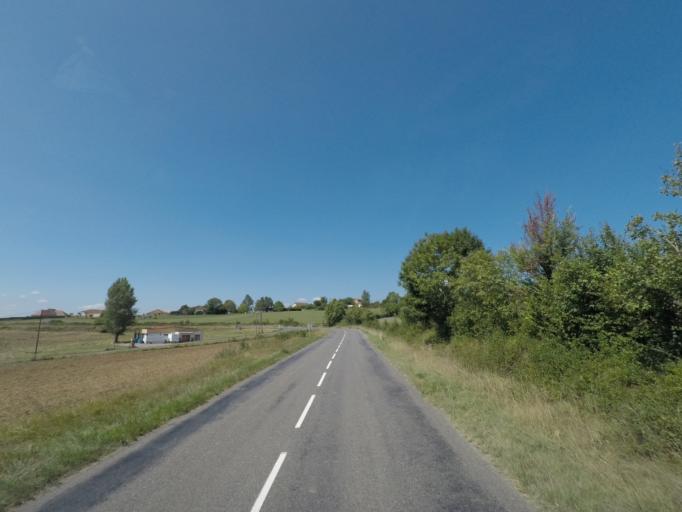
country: FR
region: Midi-Pyrenees
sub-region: Departement de l'Aveyron
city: Capdenac-Gare
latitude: 44.6146
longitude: 2.0878
